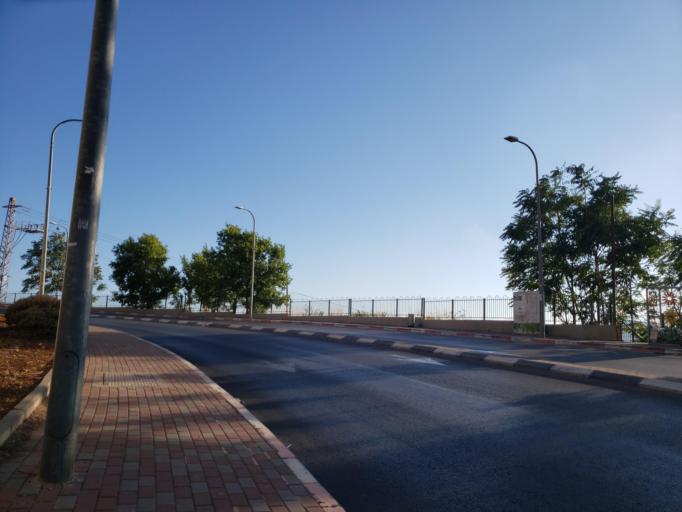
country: IL
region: Northern District
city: Safed
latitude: 32.9620
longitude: 35.4900
